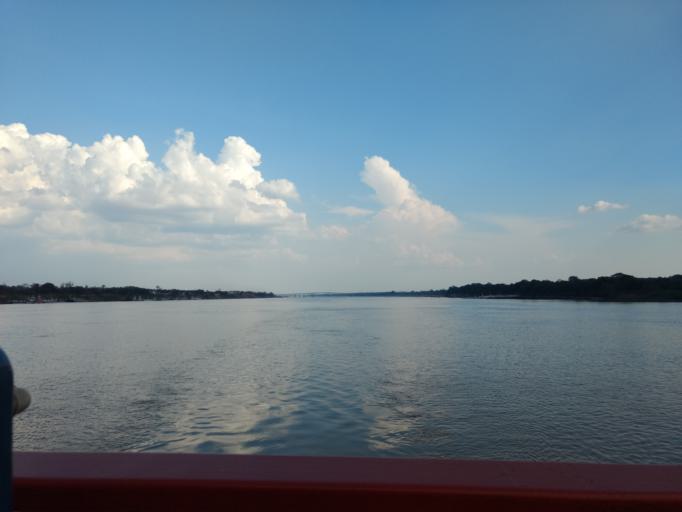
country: BR
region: Rondonia
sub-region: Porto Velho
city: Porto Velho
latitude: -8.6891
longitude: -63.9215
